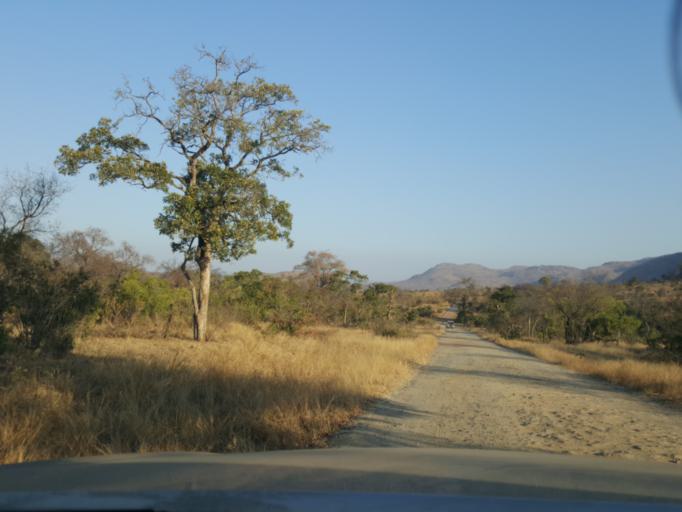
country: SZ
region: Hhohho
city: Ntfonjeni
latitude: -25.4141
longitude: 31.4410
